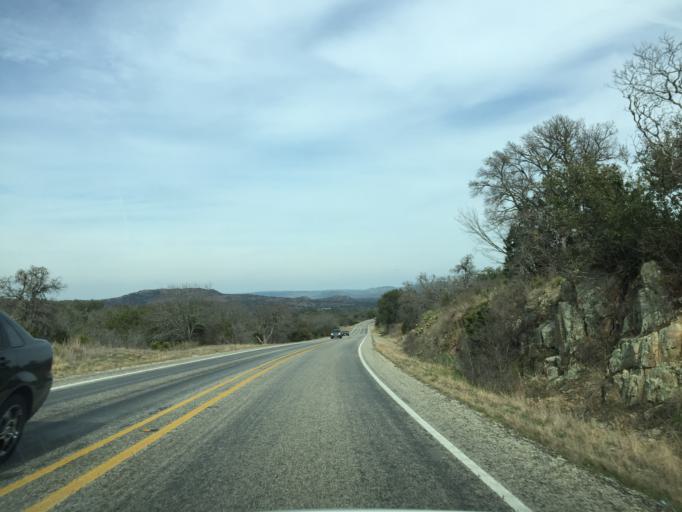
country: US
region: Texas
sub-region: Gillespie County
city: Fredericksburg
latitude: 30.4602
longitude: -98.7286
